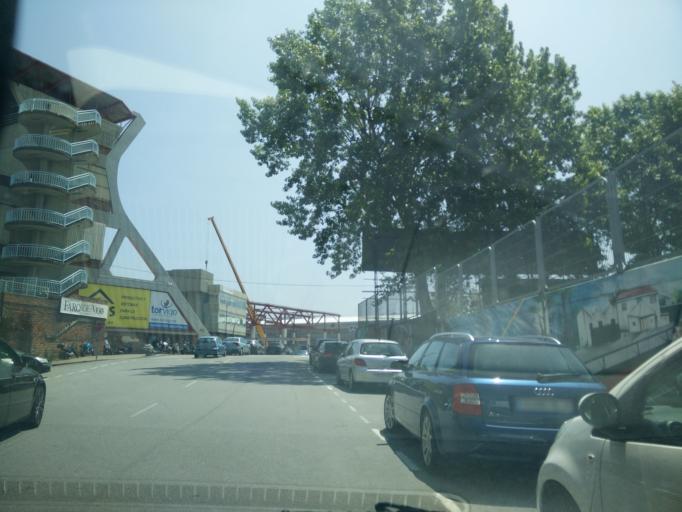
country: ES
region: Galicia
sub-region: Provincia de Pontevedra
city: Vigo
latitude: 42.2112
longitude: -8.7410
